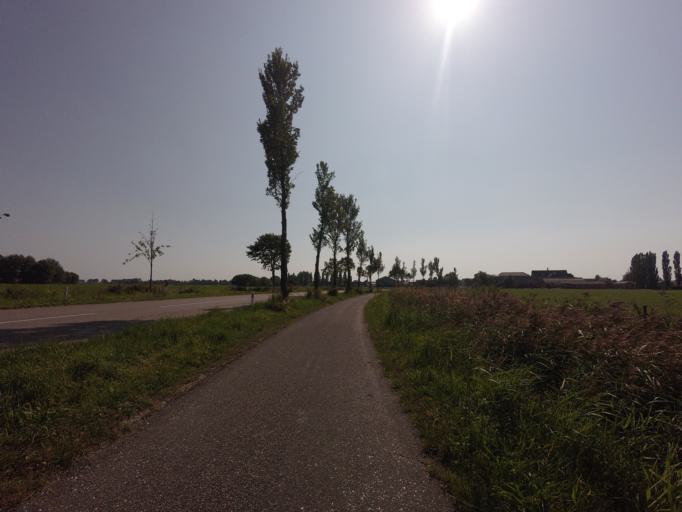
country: NL
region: Groningen
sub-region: Gemeente Zuidhorn
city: Grijpskerk
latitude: 53.2702
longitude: 6.3076
